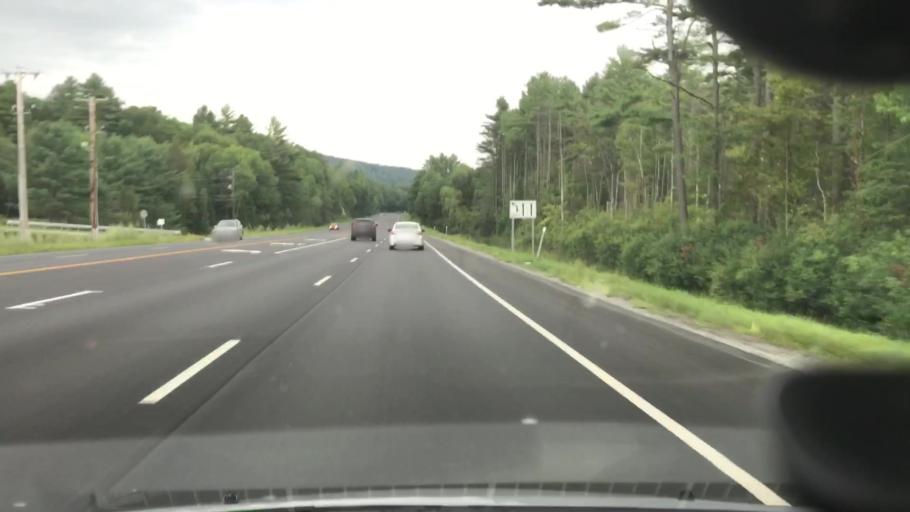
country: US
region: New Hampshire
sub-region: Grafton County
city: Lebanon
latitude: 43.6713
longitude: -72.2571
